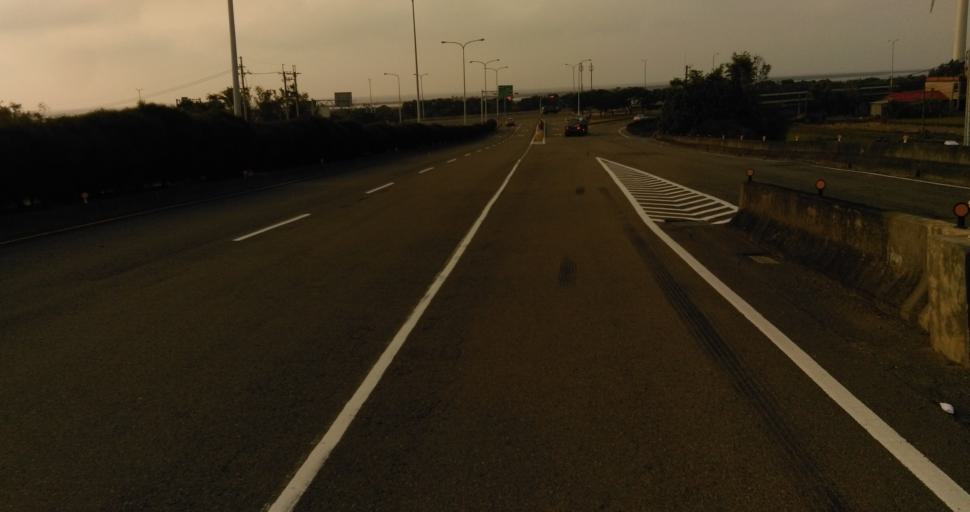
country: TW
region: Taiwan
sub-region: Hsinchu
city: Hsinchu
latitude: 24.7429
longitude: 120.8997
